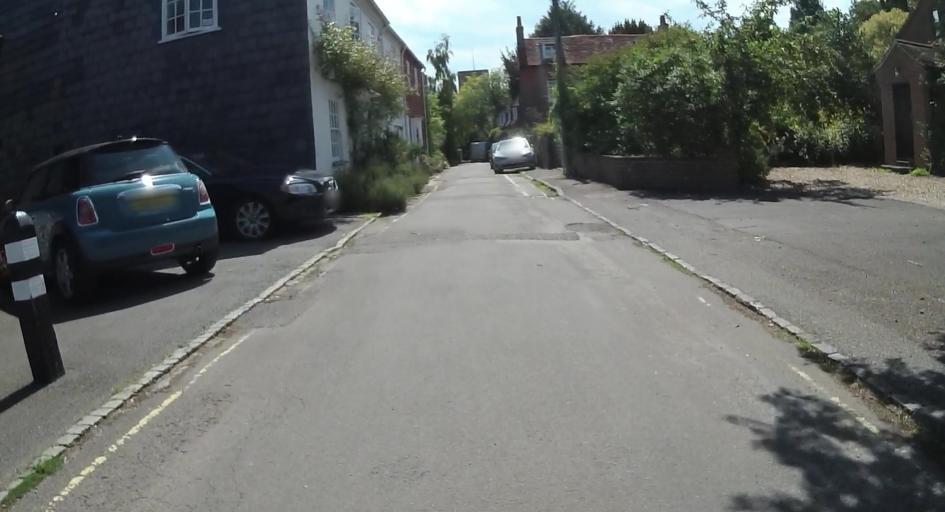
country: GB
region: England
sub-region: Hampshire
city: Winchester
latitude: 51.0490
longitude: -1.3213
